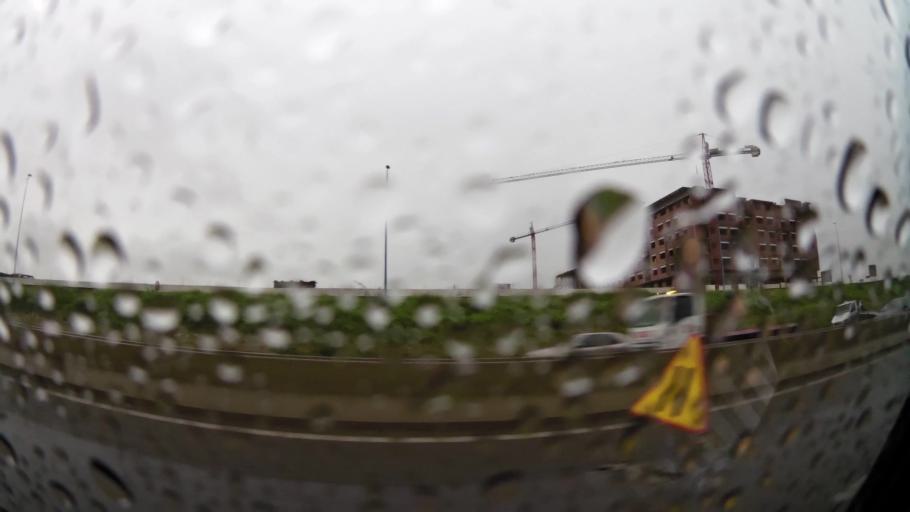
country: MA
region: Grand Casablanca
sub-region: Mediouna
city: Tit Mellil
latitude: 33.5921
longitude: -7.5269
